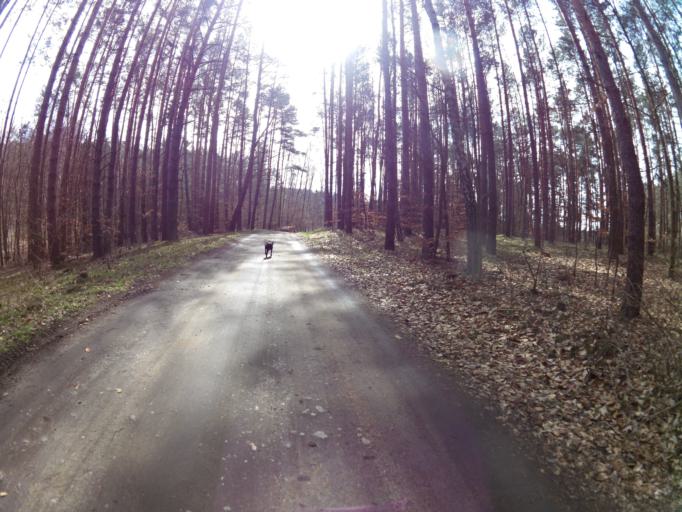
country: PL
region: West Pomeranian Voivodeship
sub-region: Powiat mysliborski
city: Mysliborz
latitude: 52.8545
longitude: 14.8404
